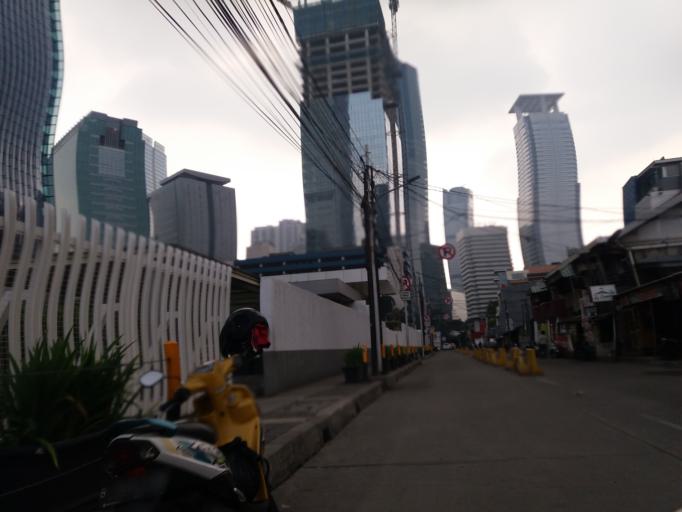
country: ID
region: Jakarta Raya
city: Jakarta
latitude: -6.2153
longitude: 106.8219
